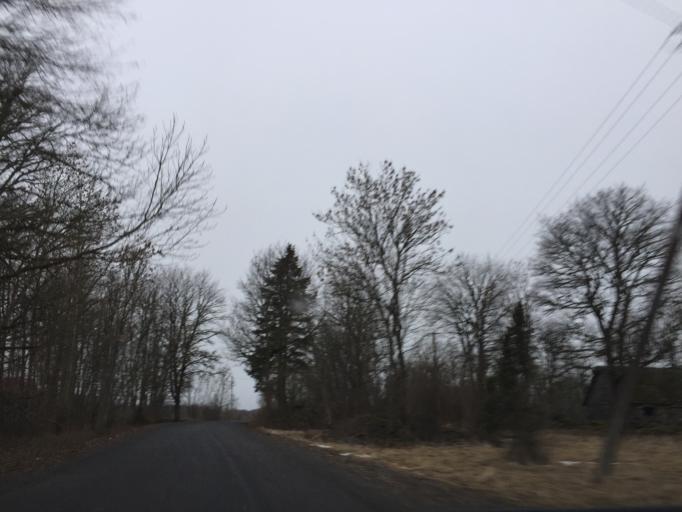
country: EE
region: Laeaene
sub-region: Lihula vald
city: Lihula
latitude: 58.6555
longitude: 23.6007
